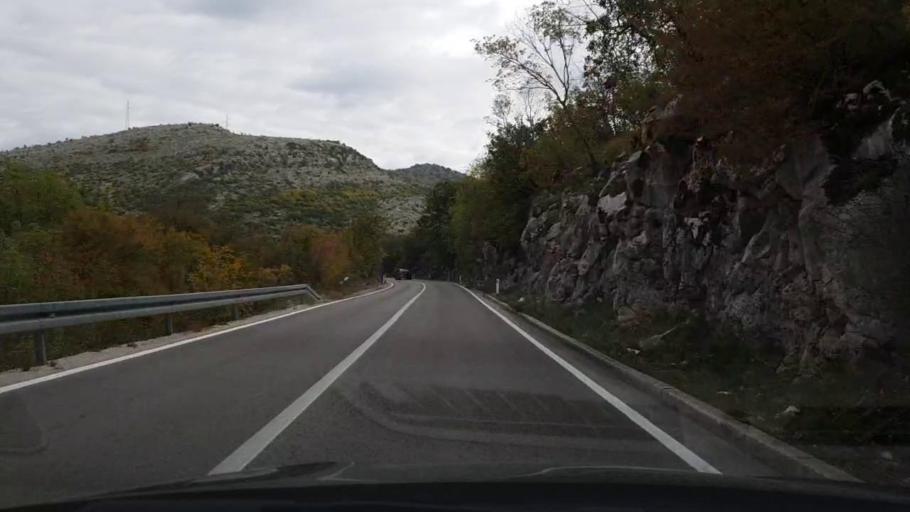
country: BA
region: Republika Srpska
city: Trebinje
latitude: 42.6821
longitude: 18.2975
